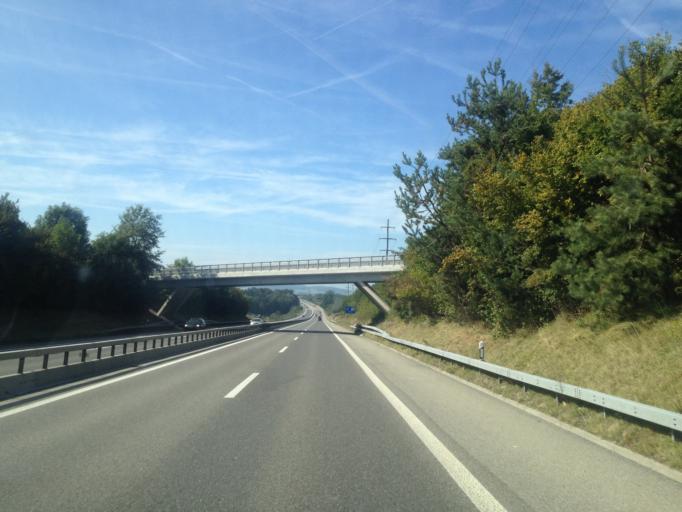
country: CH
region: Fribourg
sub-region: Sense District
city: Schmitten
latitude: 46.8708
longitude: 7.2427
